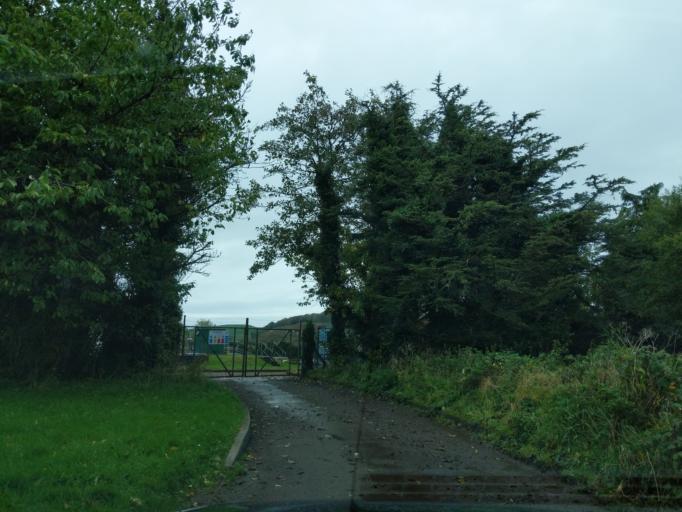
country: GB
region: Scotland
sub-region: Dumfries and Galloway
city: Kirkcudbright
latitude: 54.8365
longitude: -4.0614
